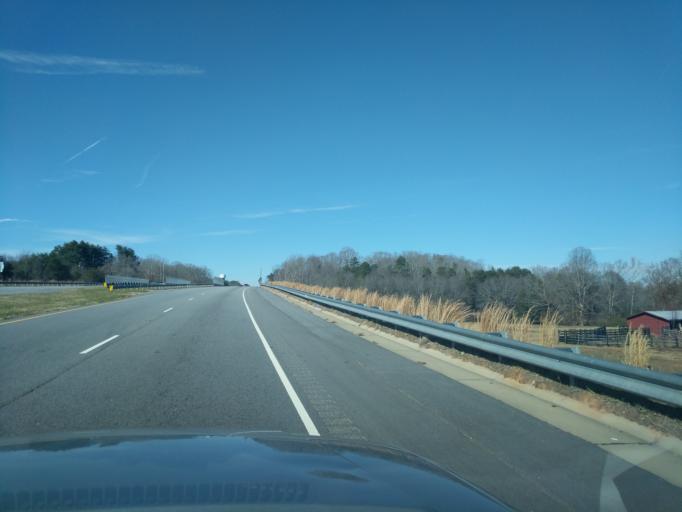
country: US
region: North Carolina
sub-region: Rutherford County
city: Forest City
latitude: 35.2478
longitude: -81.8703
